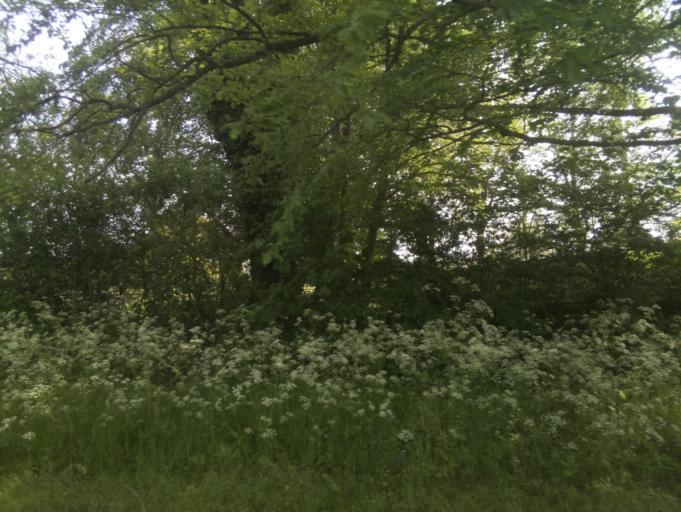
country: GB
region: England
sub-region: South Gloucestershire
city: Horton
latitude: 51.5423
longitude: -2.3593
